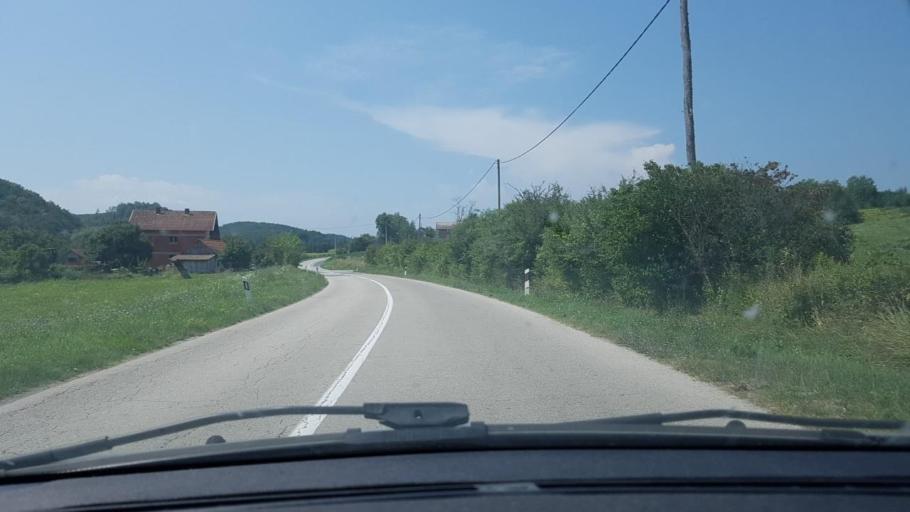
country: BA
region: Federation of Bosnia and Herzegovina
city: Velika Kladusa
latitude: 45.2160
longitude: 15.7433
